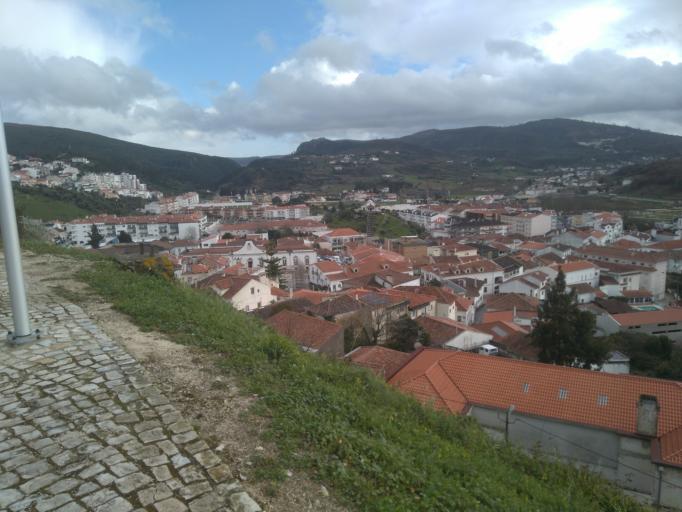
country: PT
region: Leiria
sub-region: Porto de Mos
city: Porto de Mos
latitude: 39.6034
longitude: -8.8187
